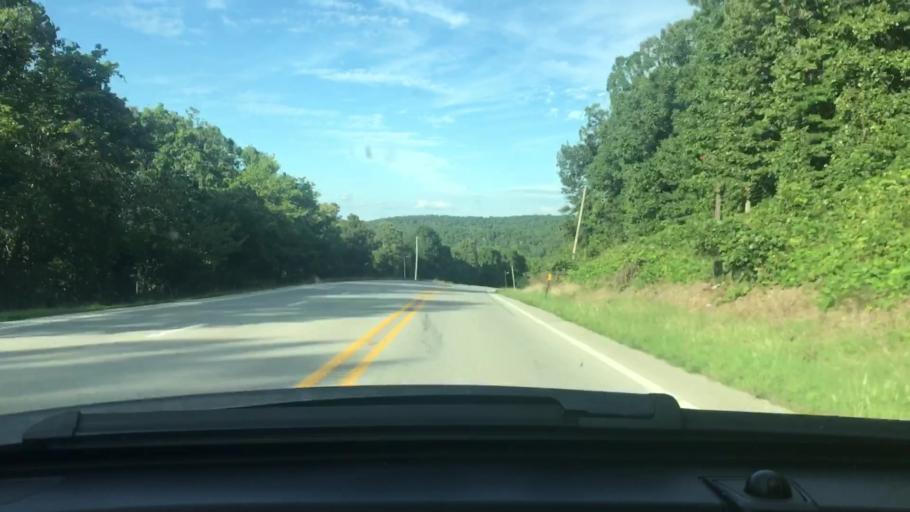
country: US
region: Arkansas
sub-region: Sharp County
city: Cherokee Village
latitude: 36.2727
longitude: -91.3664
